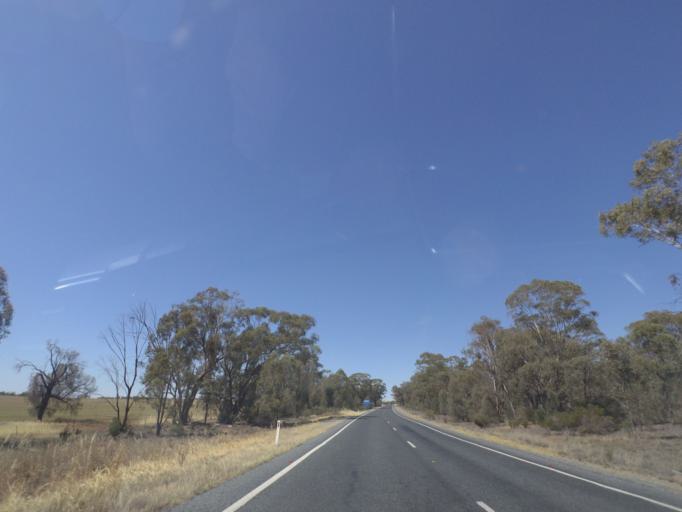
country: AU
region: New South Wales
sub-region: Narrandera
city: Narrandera
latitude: -34.4410
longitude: 146.8413
